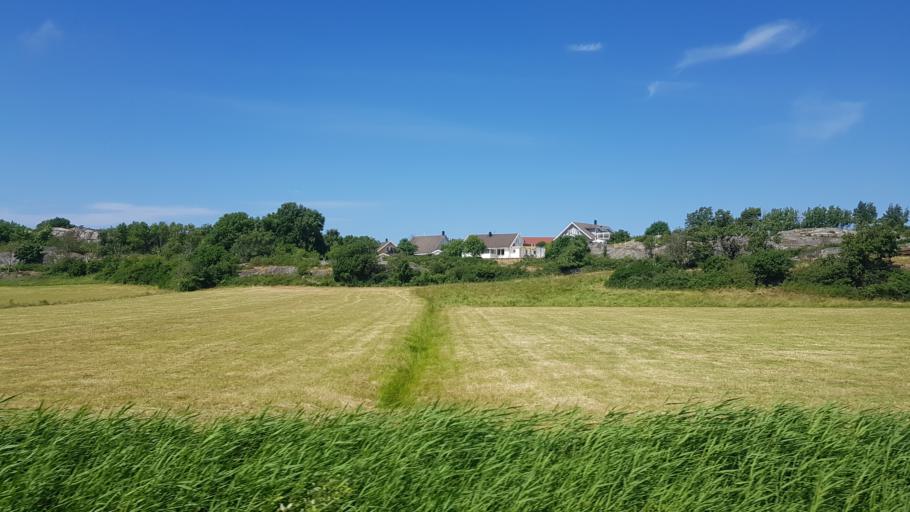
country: SE
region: Vaestra Goetaland
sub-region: Tjorns Kommun
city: Skaerhamn
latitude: 57.9824
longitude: 11.5674
